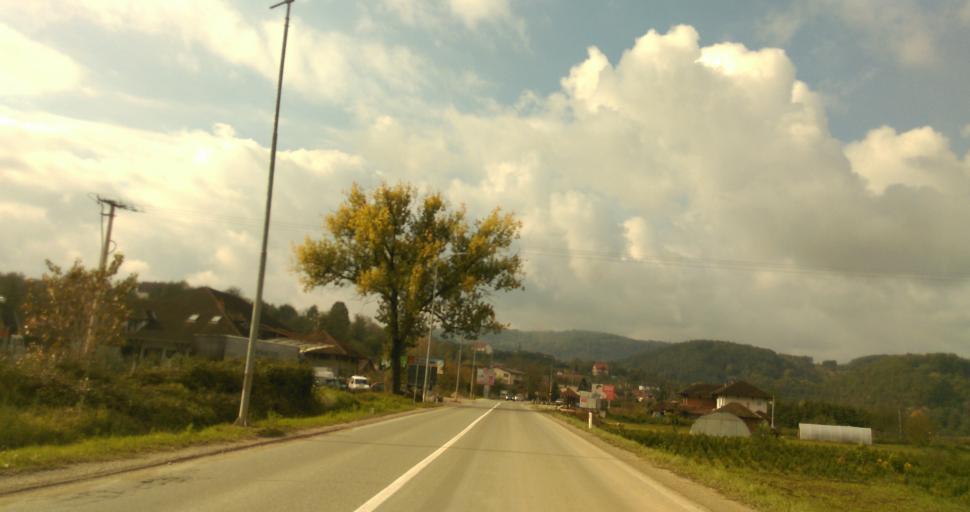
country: RS
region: Central Serbia
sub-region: Kolubarski Okrug
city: Ljig
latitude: 44.2232
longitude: 20.2364
